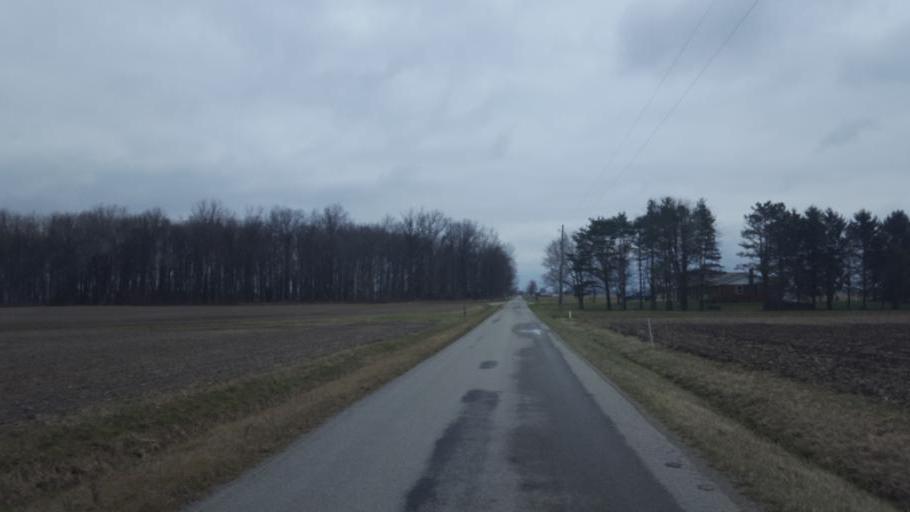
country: US
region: Ohio
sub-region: Delaware County
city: Ashley
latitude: 40.4597
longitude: -82.9890
